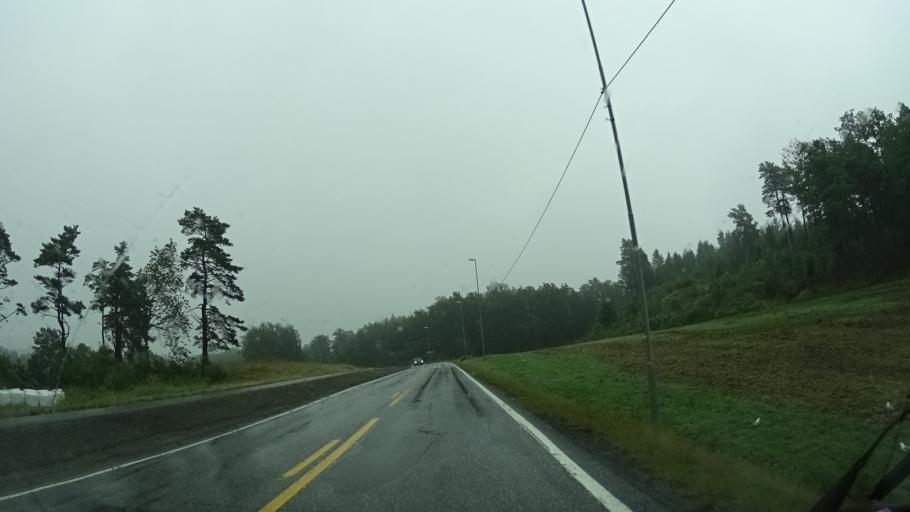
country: NO
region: Aust-Agder
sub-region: Lillesand
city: Lillesand
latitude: 58.2355
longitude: 8.3284
